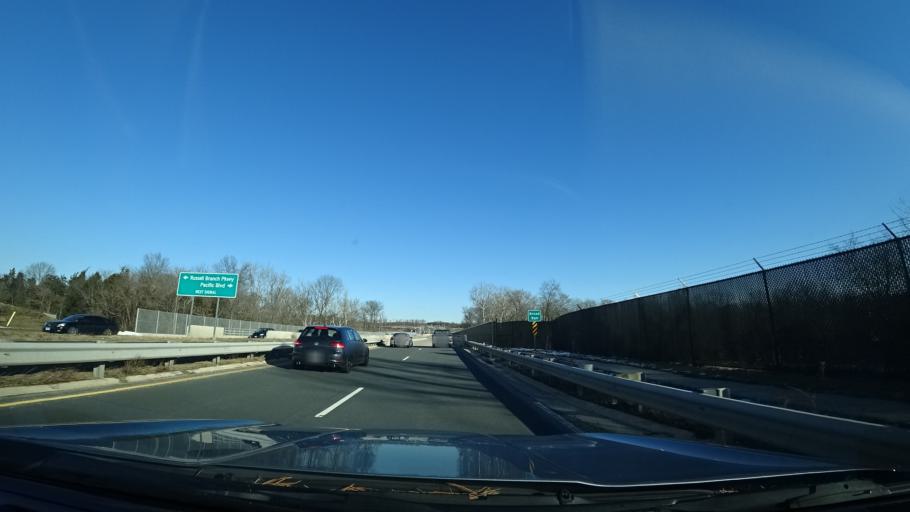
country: US
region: Virginia
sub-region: Loudoun County
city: Sterling
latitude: 39.0281
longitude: -77.4431
